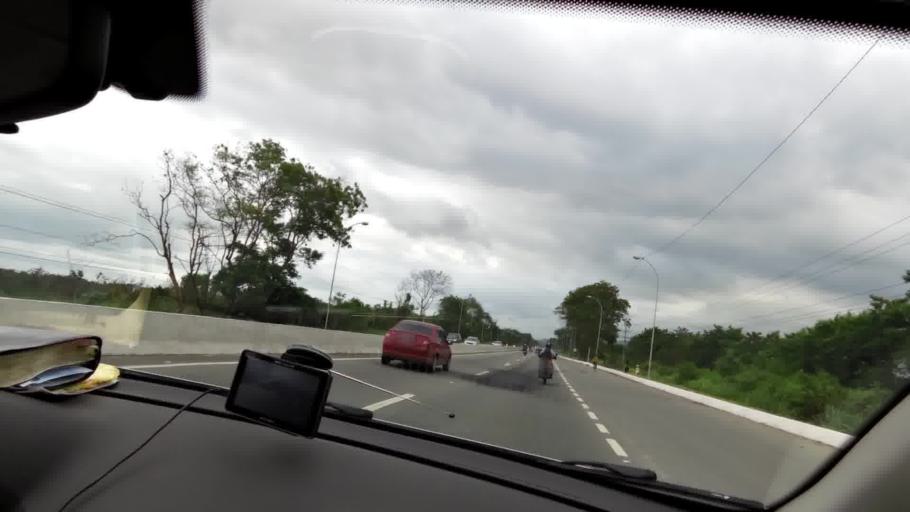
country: BR
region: Espirito Santo
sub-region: Vila Velha
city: Vila Velha
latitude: -20.2418
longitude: -40.2806
